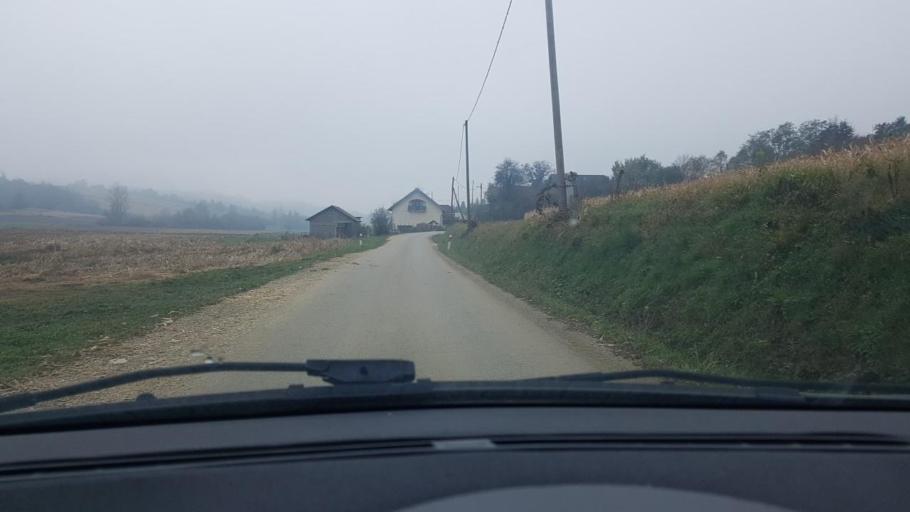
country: HR
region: Krapinsko-Zagorska
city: Zlatar
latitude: 46.1145
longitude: 16.1781
